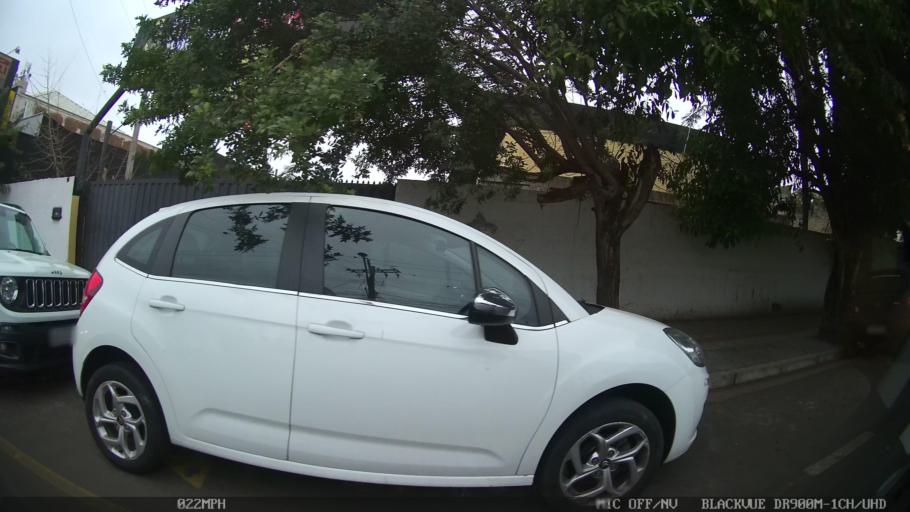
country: BR
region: Sao Paulo
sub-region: Sao Jose Do Rio Preto
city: Sao Jose do Rio Preto
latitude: -20.8224
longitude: -49.3937
